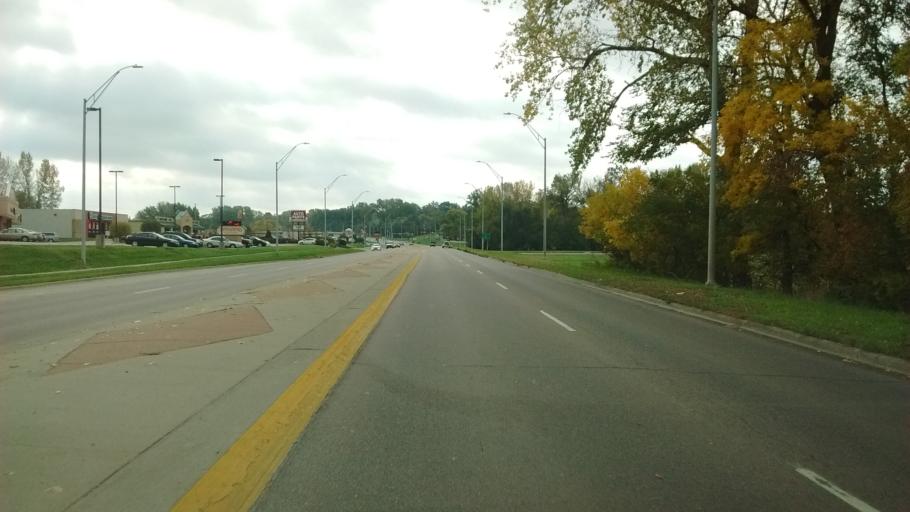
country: US
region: Iowa
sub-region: Woodbury County
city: Sioux City
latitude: 42.4823
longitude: -96.3543
